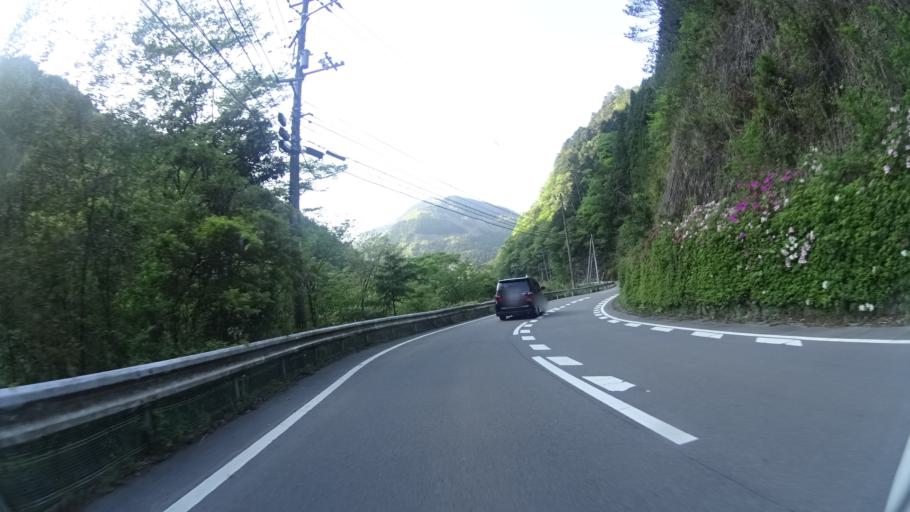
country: JP
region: Tokushima
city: Ikedacho
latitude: 33.8724
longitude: 133.8698
